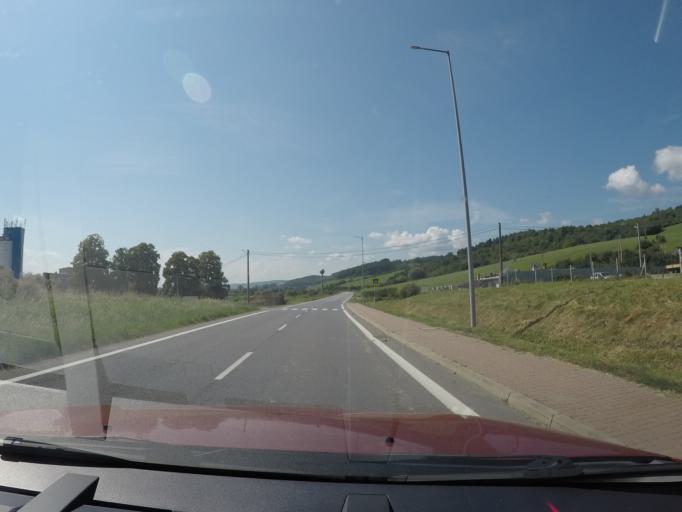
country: SK
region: Presovsky
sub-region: Okres Presov
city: Presov
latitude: 48.9209
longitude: 21.2410
